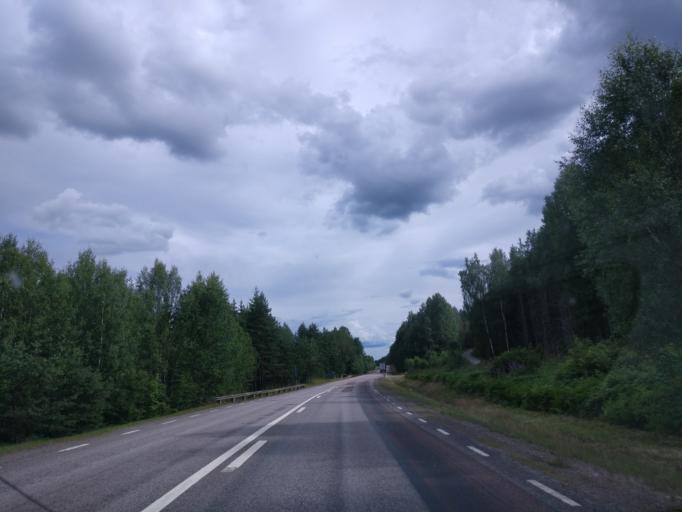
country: SE
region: Vaermland
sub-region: Hagfors Kommun
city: Ekshaerad
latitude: 60.1559
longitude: 13.5159
